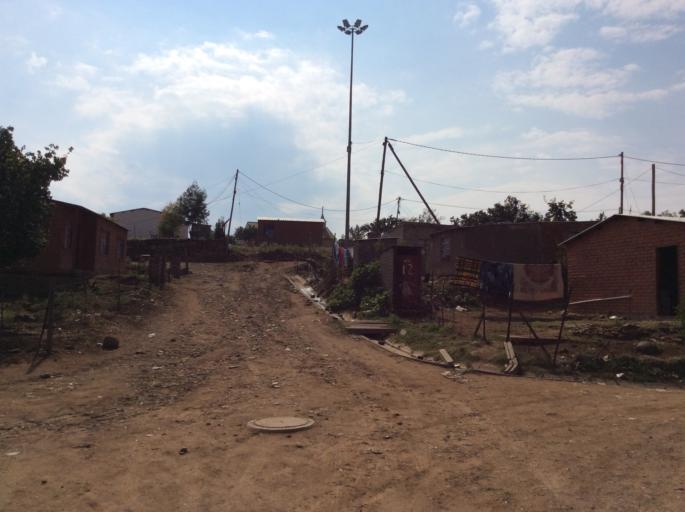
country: LS
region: Mafeteng
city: Mafeteng
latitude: -29.9836
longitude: 27.0044
